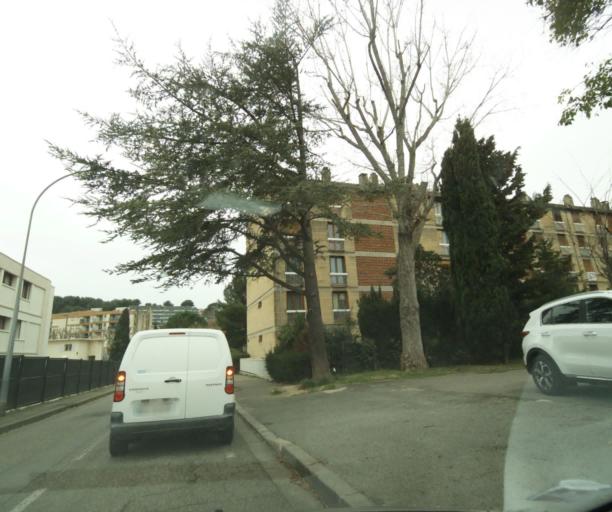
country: FR
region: Provence-Alpes-Cote d'Azur
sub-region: Departement des Bouches-du-Rhone
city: Aix-en-Provence
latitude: 43.5183
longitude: 5.4599
